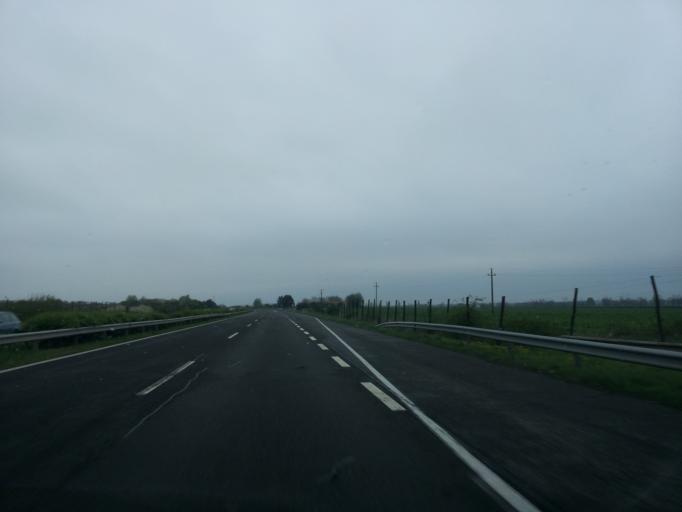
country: HU
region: Heves
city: Hort
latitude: 47.7071
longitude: 19.8066
